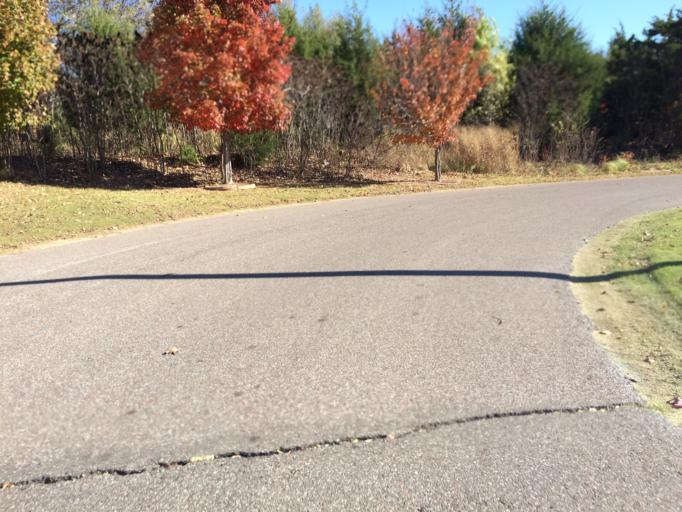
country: US
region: Oklahoma
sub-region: Cleveland County
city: Noble
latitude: 35.1647
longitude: -97.4196
